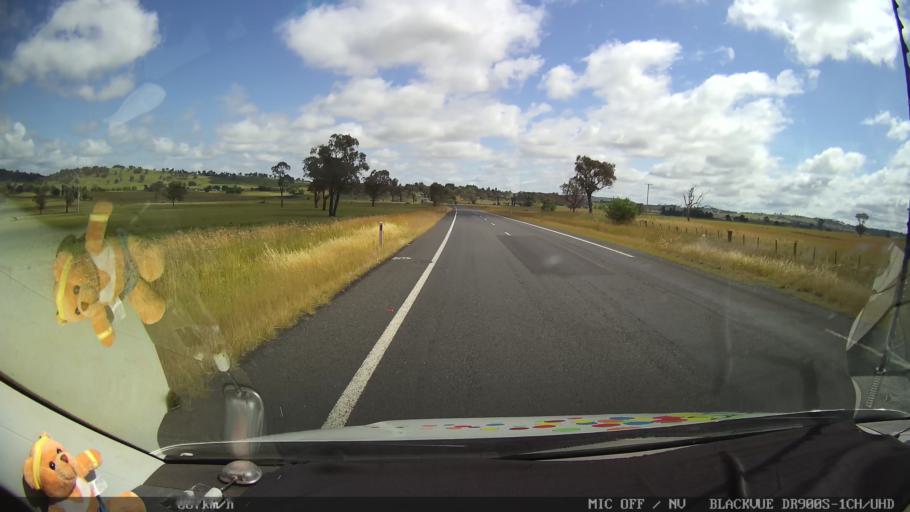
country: AU
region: New South Wales
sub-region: Glen Innes Severn
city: Glen Innes
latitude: -29.9410
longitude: 151.7228
